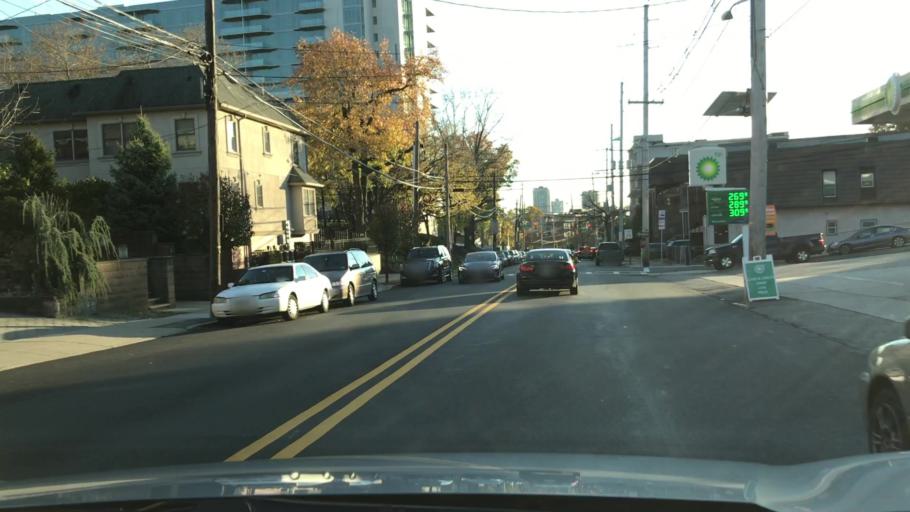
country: US
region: New Jersey
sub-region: Bergen County
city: Cliffside Park
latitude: 40.8158
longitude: -73.9893
